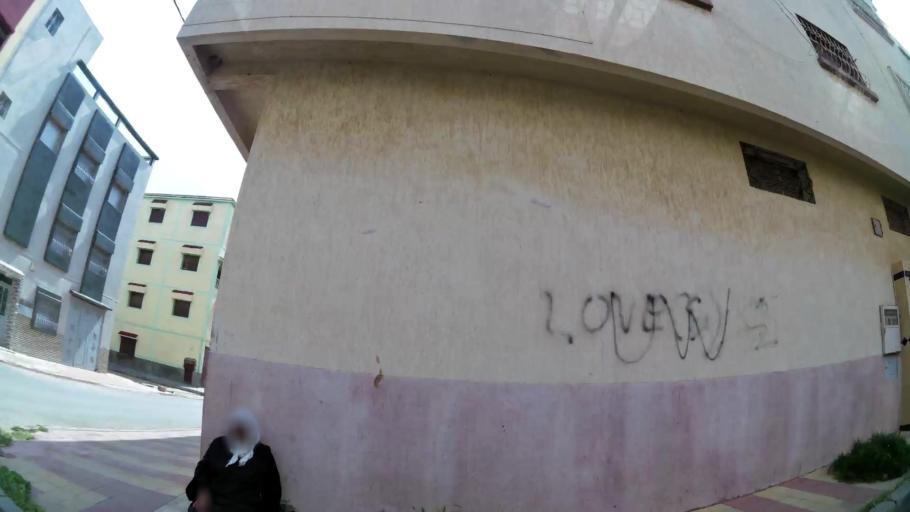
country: MA
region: Rabat-Sale-Zemmour-Zaer
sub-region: Khemisset
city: Tiflet
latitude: 33.8948
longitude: -6.3285
